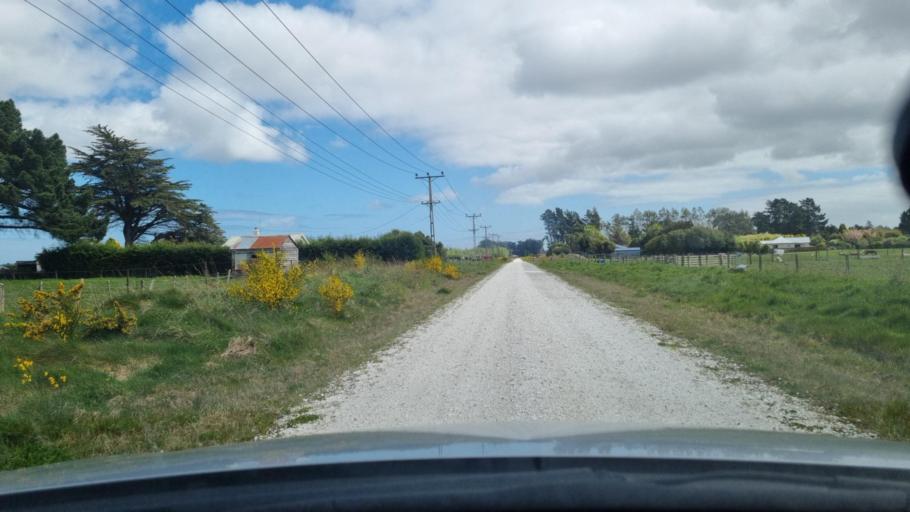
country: NZ
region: Southland
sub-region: Invercargill City
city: Invercargill
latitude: -46.4431
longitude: 168.3917
